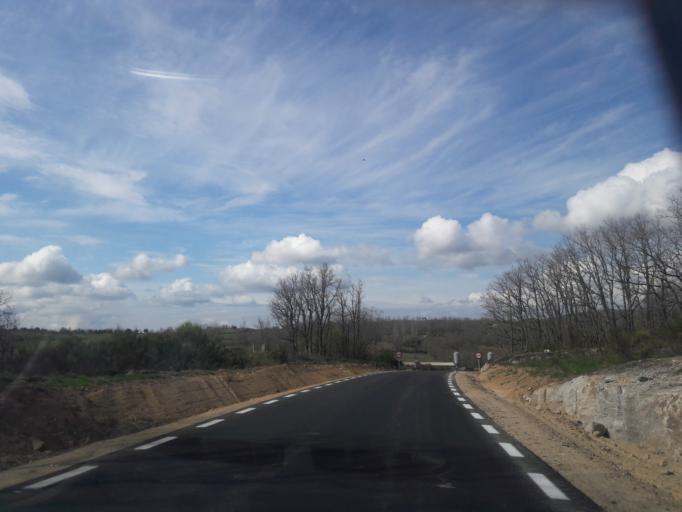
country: ES
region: Castille and Leon
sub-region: Provincia de Salamanca
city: Valdefuentes de Sangusin
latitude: 40.5191
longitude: -5.8481
